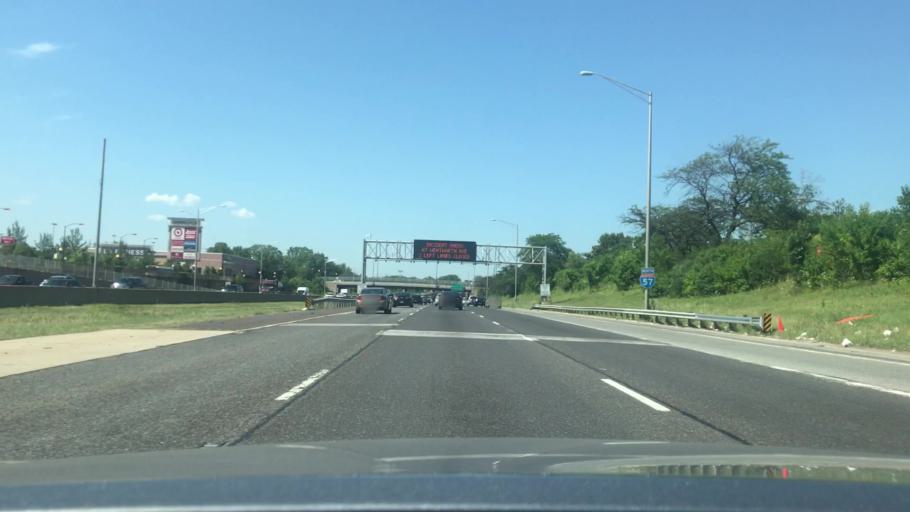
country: US
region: Illinois
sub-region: Cook County
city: Calumet Park
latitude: 41.6815
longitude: -87.6619
